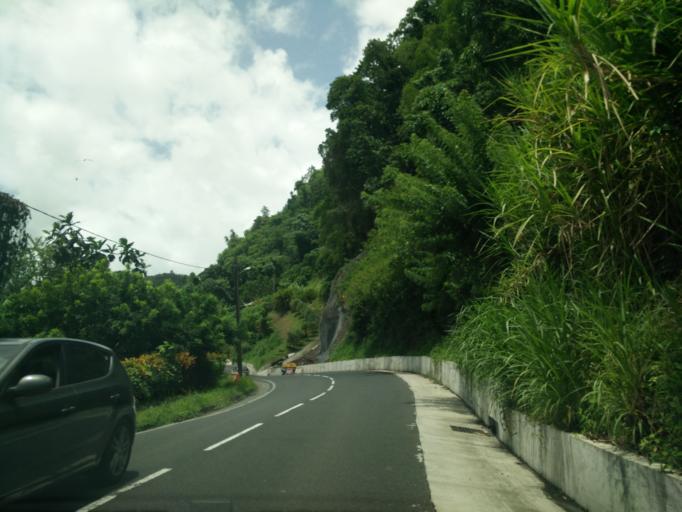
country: MQ
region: Martinique
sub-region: Martinique
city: Saint-Pierre
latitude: 14.7517
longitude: -61.1656
